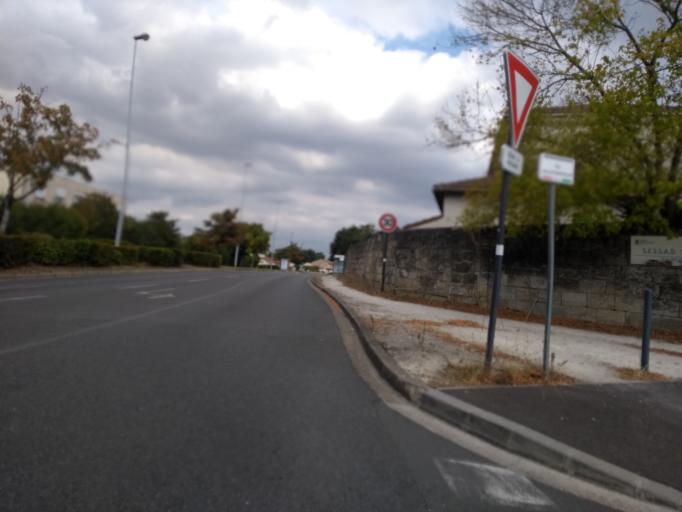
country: FR
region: Aquitaine
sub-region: Departement de la Gironde
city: Talence
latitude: 44.7960
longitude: -0.5816
